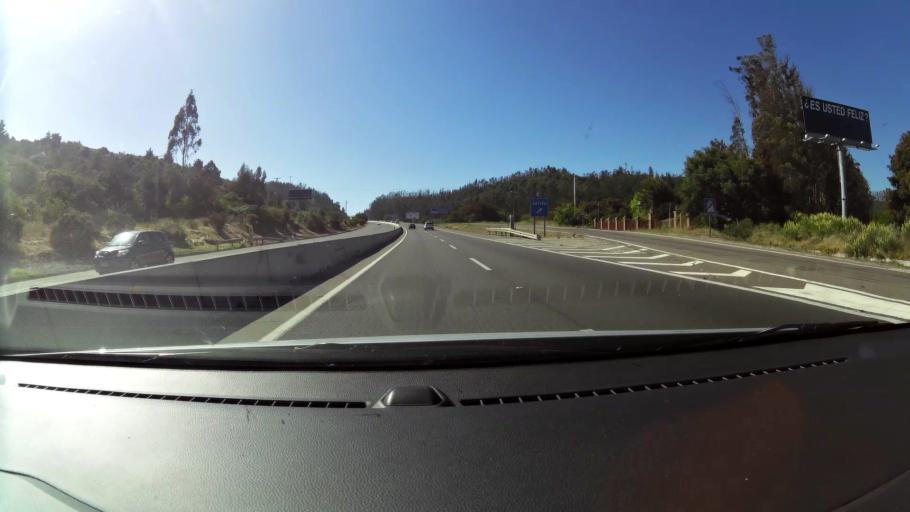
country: CL
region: Valparaiso
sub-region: Provincia de Marga Marga
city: Quilpue
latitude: -33.2146
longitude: -71.4746
